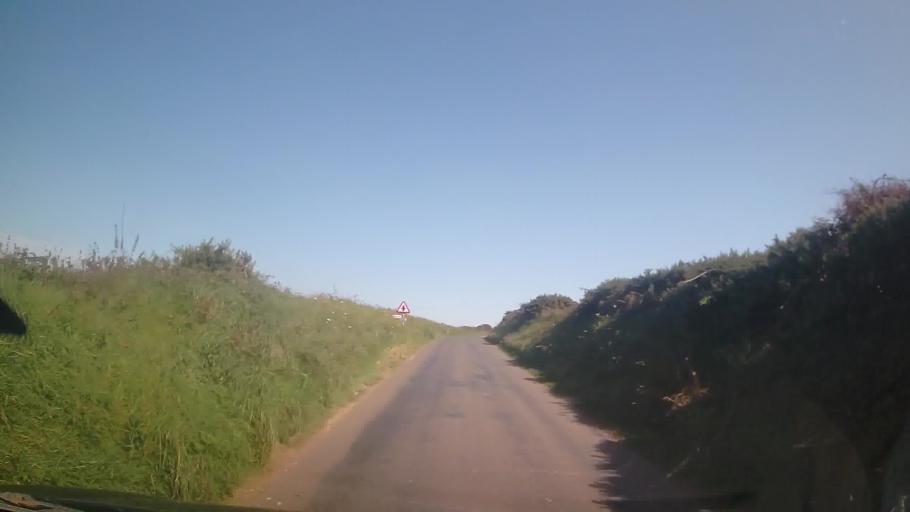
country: GB
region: Wales
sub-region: Pembrokeshire
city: Llanrhian
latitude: 51.9307
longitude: -5.1898
